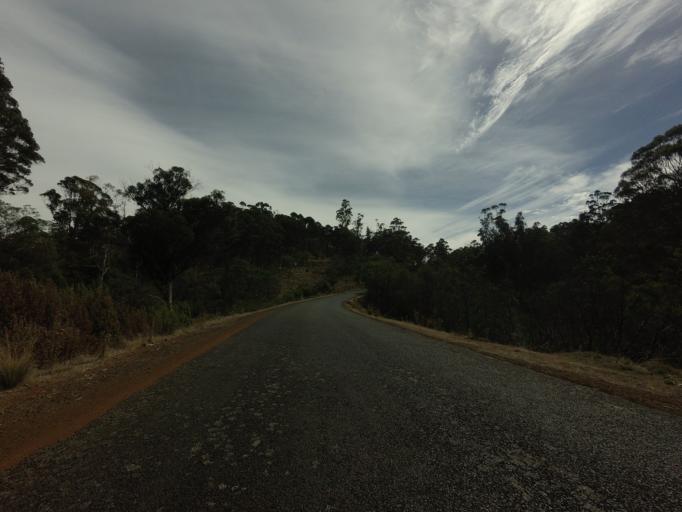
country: AU
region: Tasmania
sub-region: Sorell
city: Sorell
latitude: -42.5651
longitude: 147.6816
